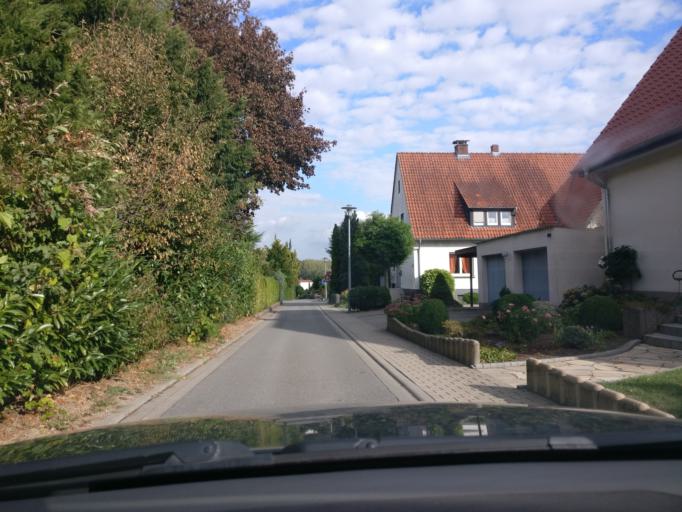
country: DE
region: Lower Saxony
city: Melle
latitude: 52.1866
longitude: 8.3462
